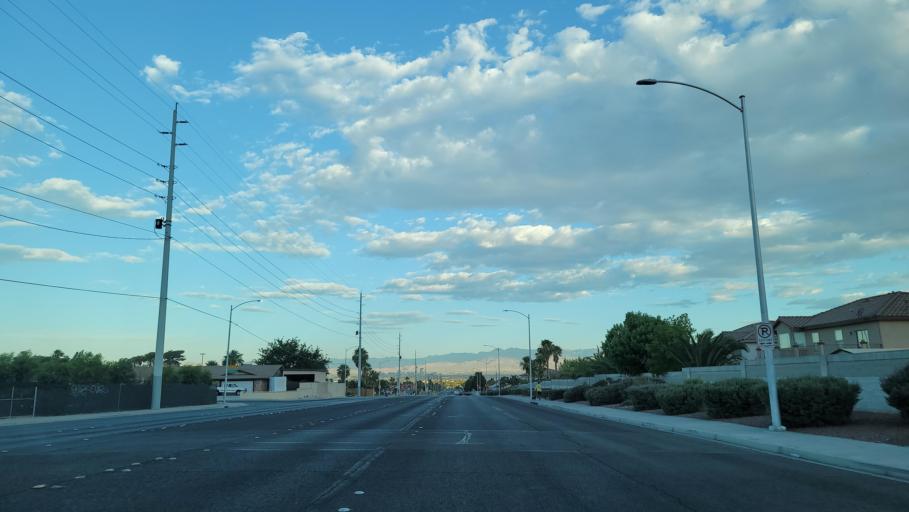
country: US
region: Nevada
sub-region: Clark County
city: Sunrise Manor
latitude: 36.1741
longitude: -115.0317
